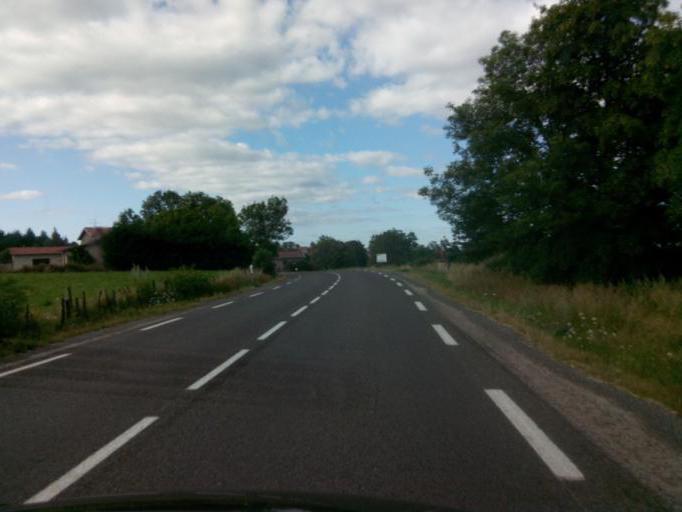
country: FR
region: Auvergne
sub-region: Departement de la Haute-Loire
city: Saint-Paulien
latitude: 45.2130
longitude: 3.8178
